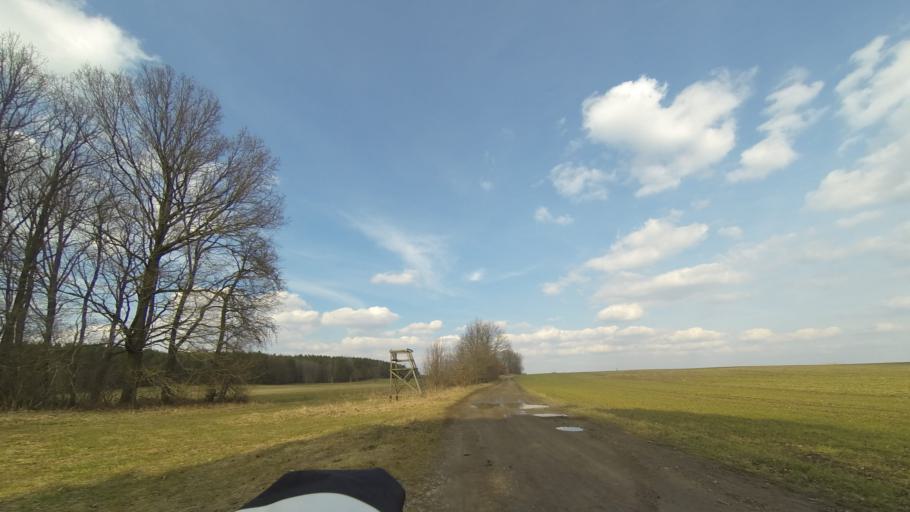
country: DE
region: Saxony
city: Ebersbach
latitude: 51.1955
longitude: 13.6616
